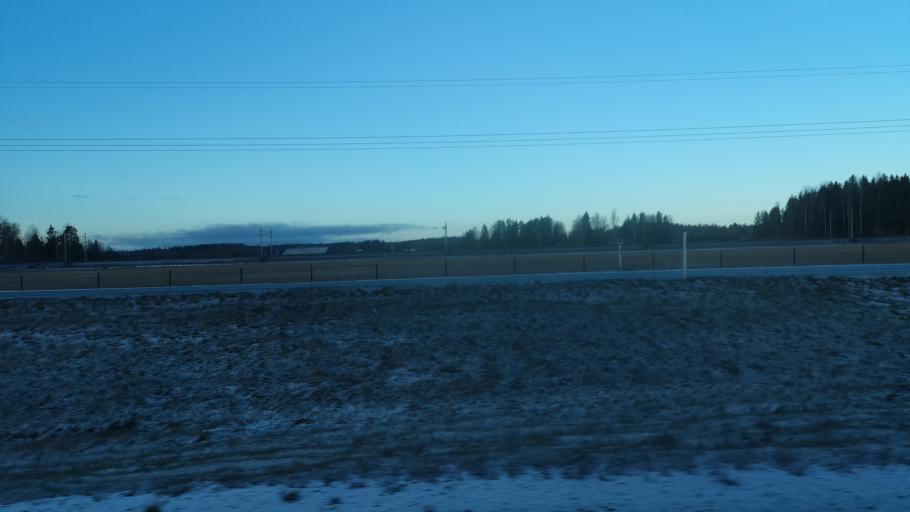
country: FI
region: Uusimaa
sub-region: Helsinki
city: Maentsaelae
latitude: 60.6105
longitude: 25.2645
